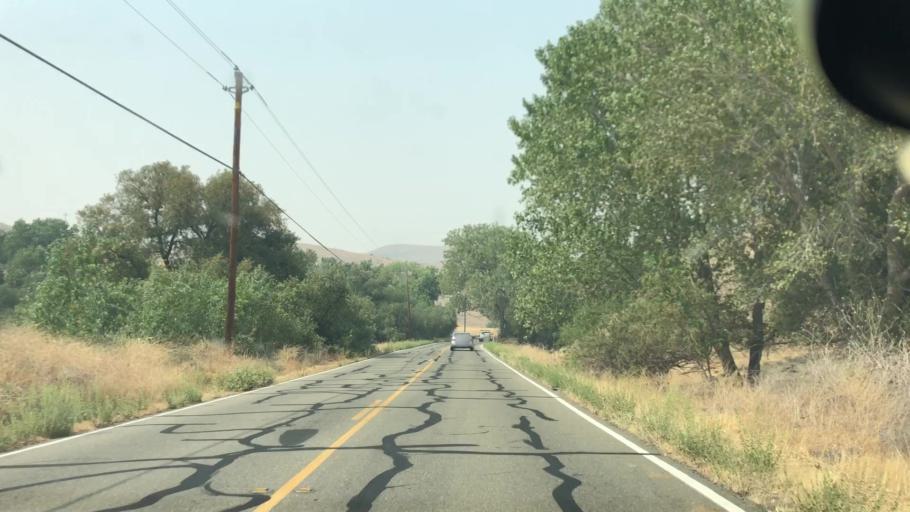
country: US
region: California
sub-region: San Joaquin County
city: Tracy
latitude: 37.6455
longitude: -121.4910
